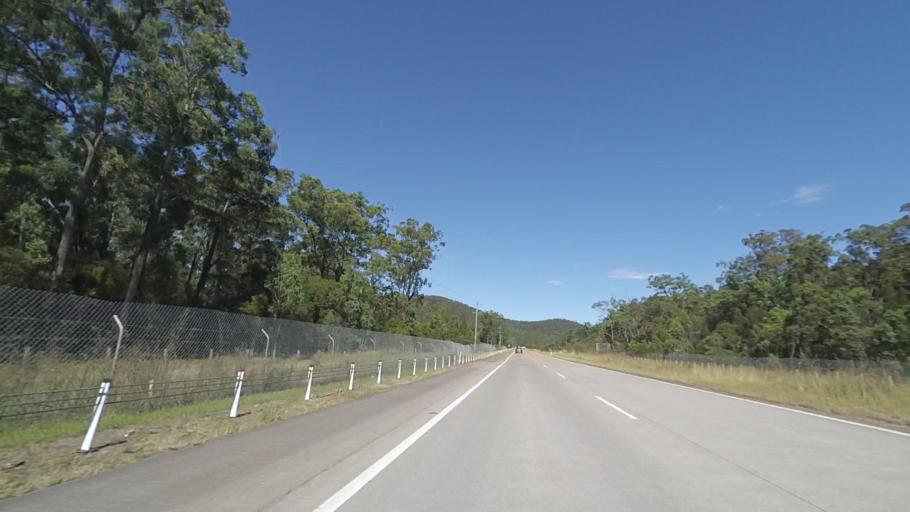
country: AU
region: New South Wales
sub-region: Port Stephens Shire
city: Port Stephens
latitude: -32.6332
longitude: 152.0056
